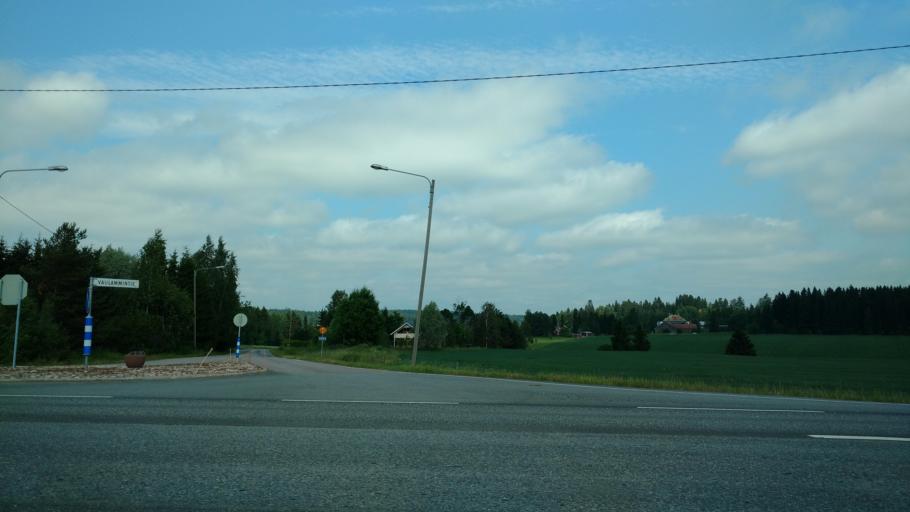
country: FI
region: Haeme
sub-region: Forssa
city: Jokioinen
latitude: 60.7807
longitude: 23.4208
